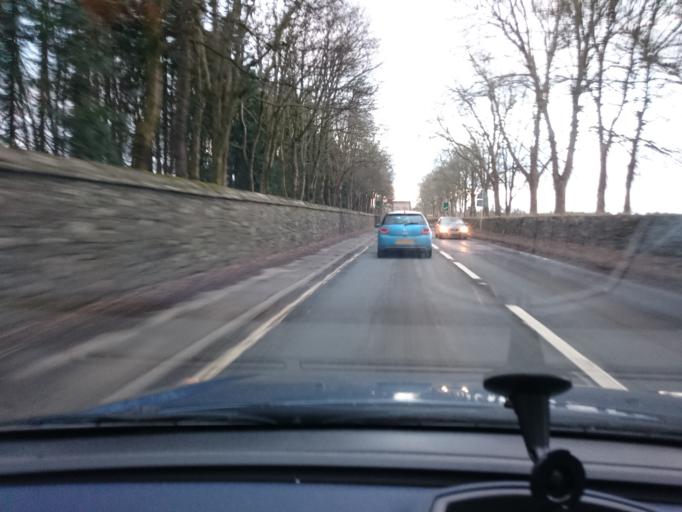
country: GB
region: Scotland
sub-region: Stirling
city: Doune
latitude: 56.2018
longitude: -4.0839
